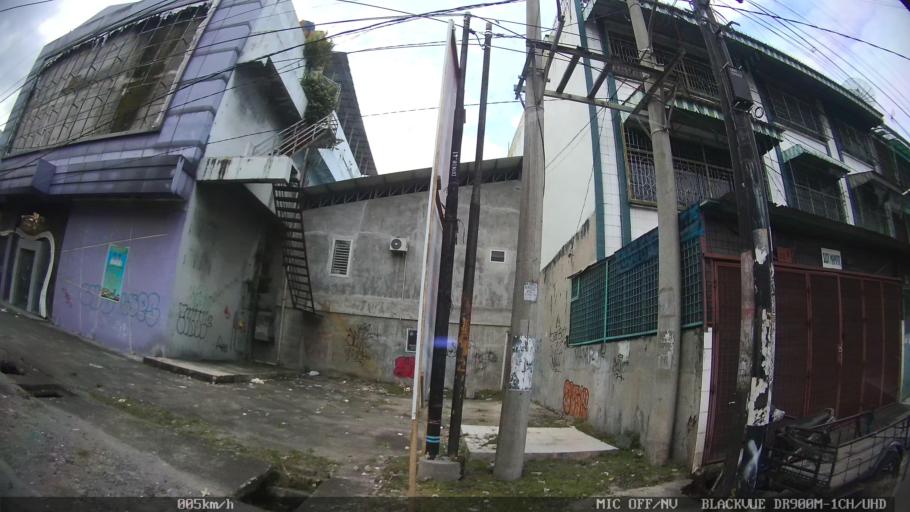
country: ID
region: North Sumatra
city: Medan
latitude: 3.6072
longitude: 98.6772
